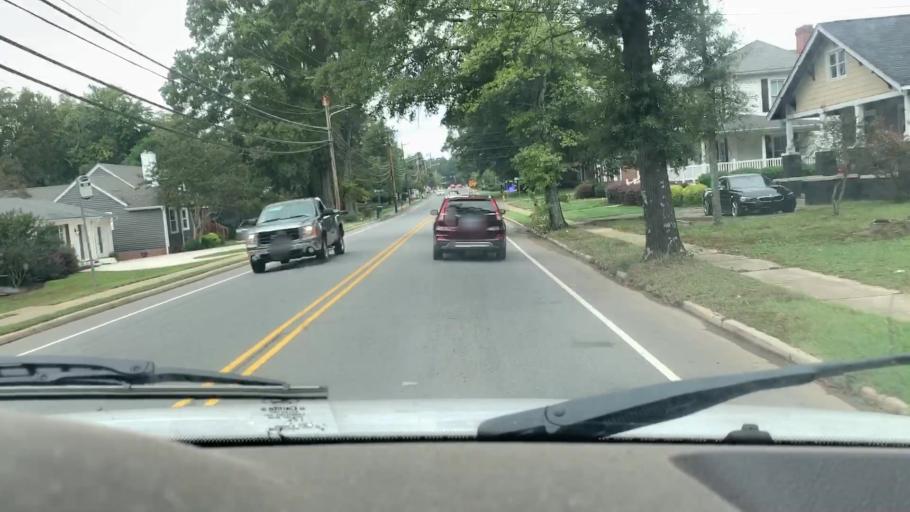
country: US
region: North Carolina
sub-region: Mecklenburg County
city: Huntersville
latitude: 35.4070
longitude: -80.8420
